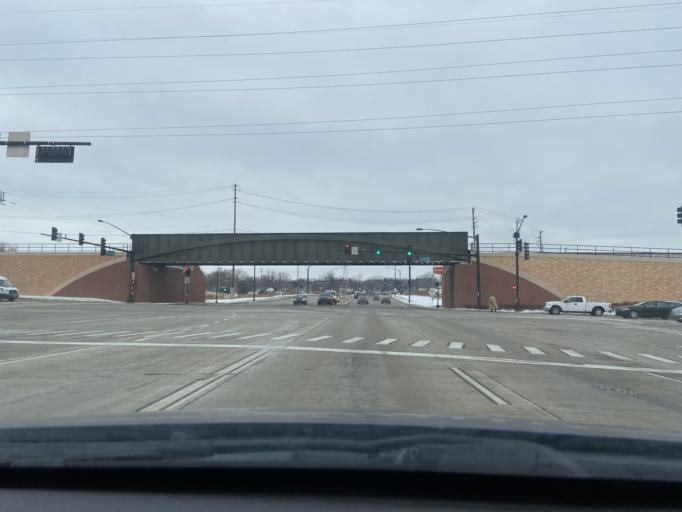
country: US
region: Illinois
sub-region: Lake County
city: Venetian Village
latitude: 42.3801
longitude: -88.0623
